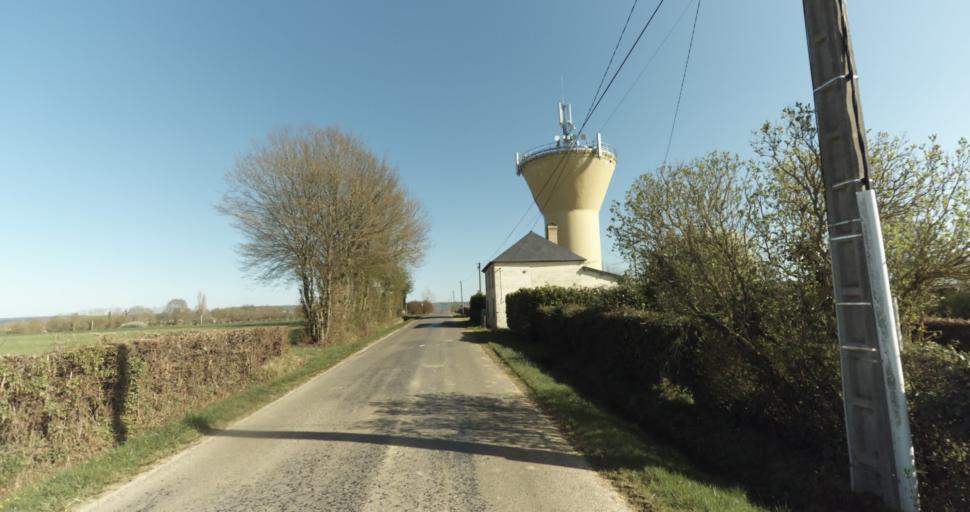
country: FR
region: Lower Normandy
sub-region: Departement du Calvados
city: Saint-Pierre-sur-Dives
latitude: 48.9400
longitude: -0.0101
